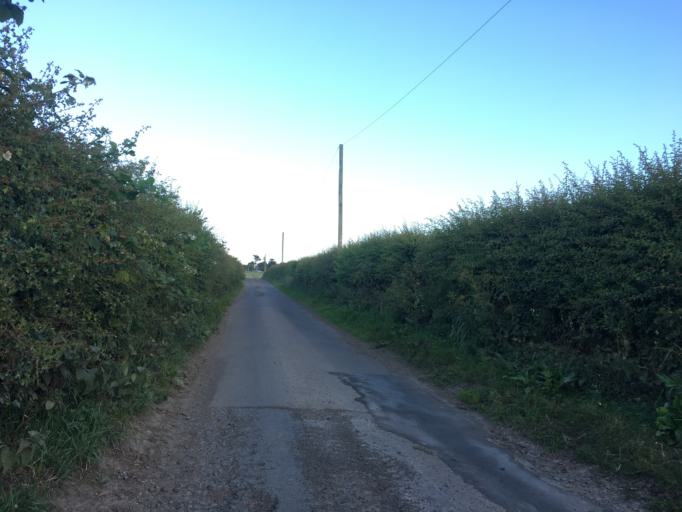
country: GB
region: England
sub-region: Northumberland
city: North Sunderland
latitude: 55.5911
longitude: -1.6858
